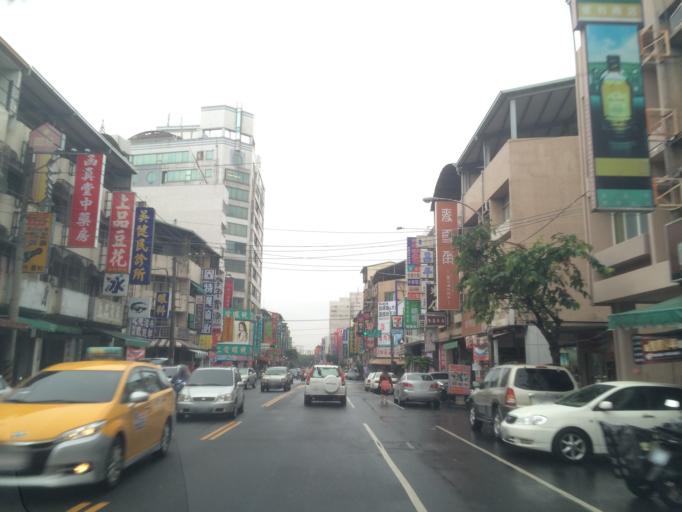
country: TW
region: Taiwan
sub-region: Taichung City
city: Taichung
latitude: 24.1763
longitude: 120.6903
